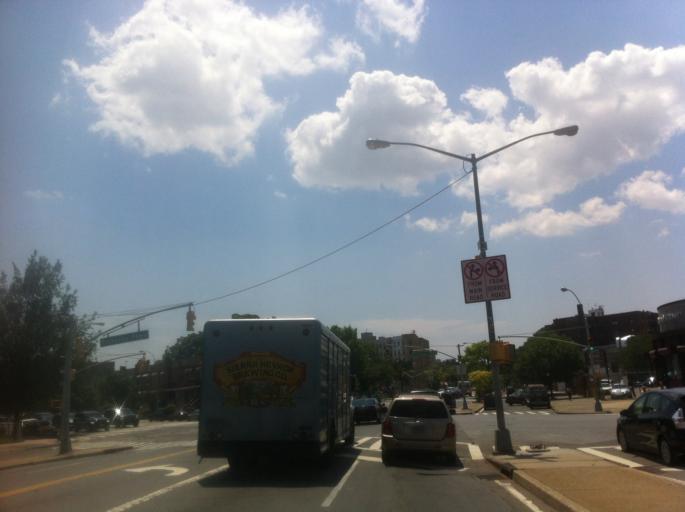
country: US
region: New York
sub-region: Kings County
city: Brooklyn
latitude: 40.6623
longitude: -73.9196
